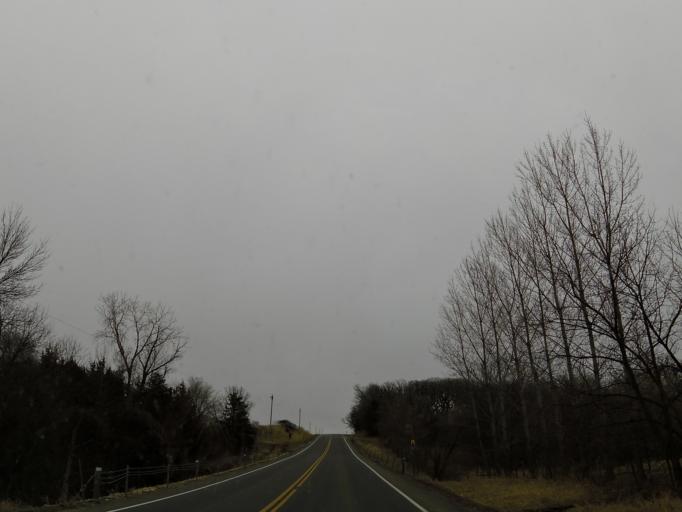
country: US
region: Minnesota
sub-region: Le Sueur County
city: Le Sueur
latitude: 44.5431
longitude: -93.8799
